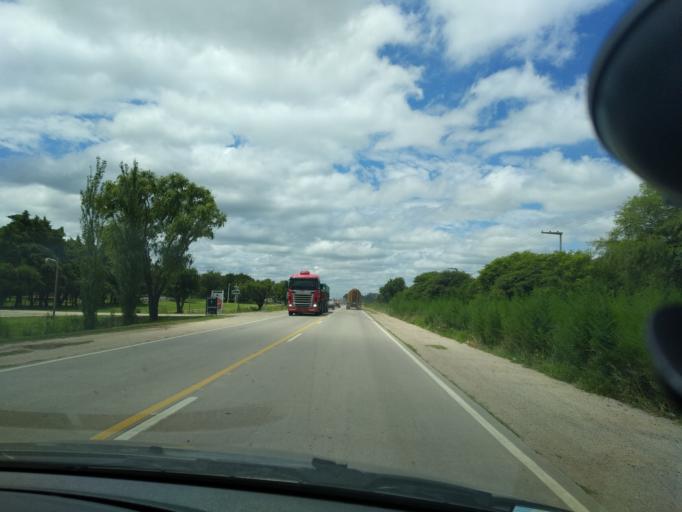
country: AR
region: Cordoba
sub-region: Departamento de Rio Segundo
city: Rio Segundo
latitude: -31.6429
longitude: -63.8985
